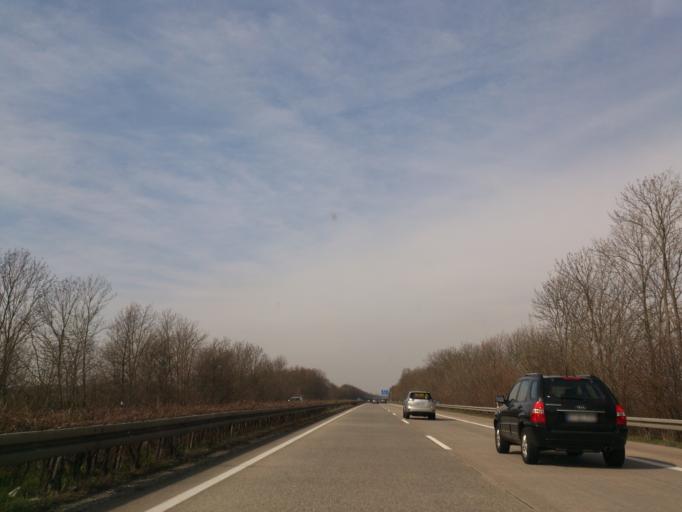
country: DE
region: North Rhine-Westphalia
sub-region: Regierungsbezirk Arnsberg
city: Anrochte
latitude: 51.5856
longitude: 8.3581
